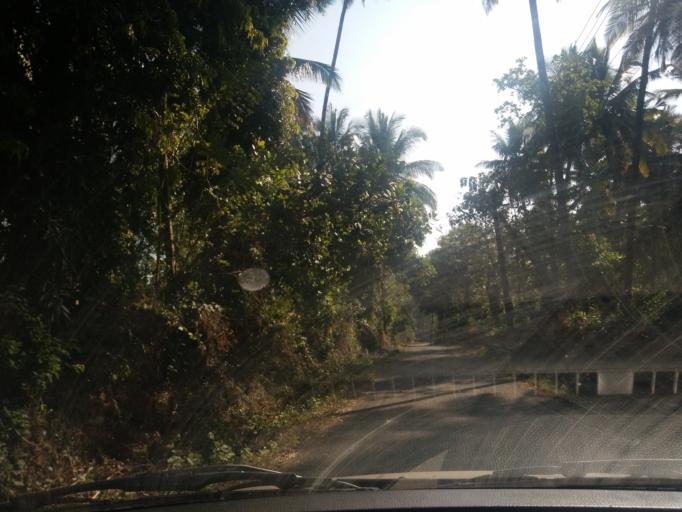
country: IN
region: Goa
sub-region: South Goa
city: Quepem
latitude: 15.1590
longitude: 74.0883
